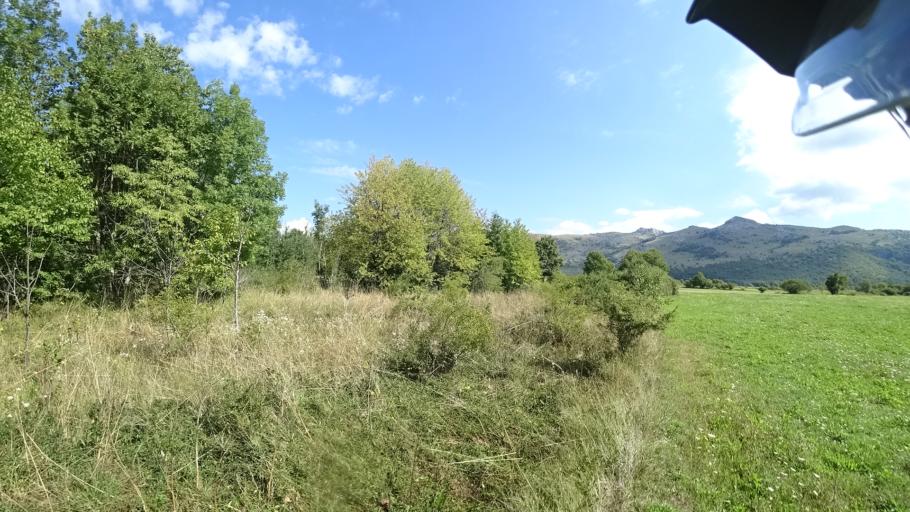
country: HR
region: Zadarska
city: Gracac
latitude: 44.3385
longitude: 15.9548
